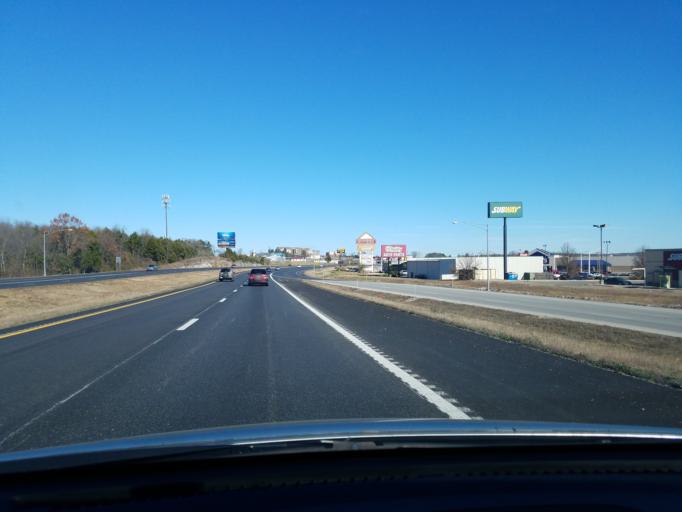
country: US
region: Missouri
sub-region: Taney County
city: Hollister
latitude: 36.6119
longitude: -93.2315
